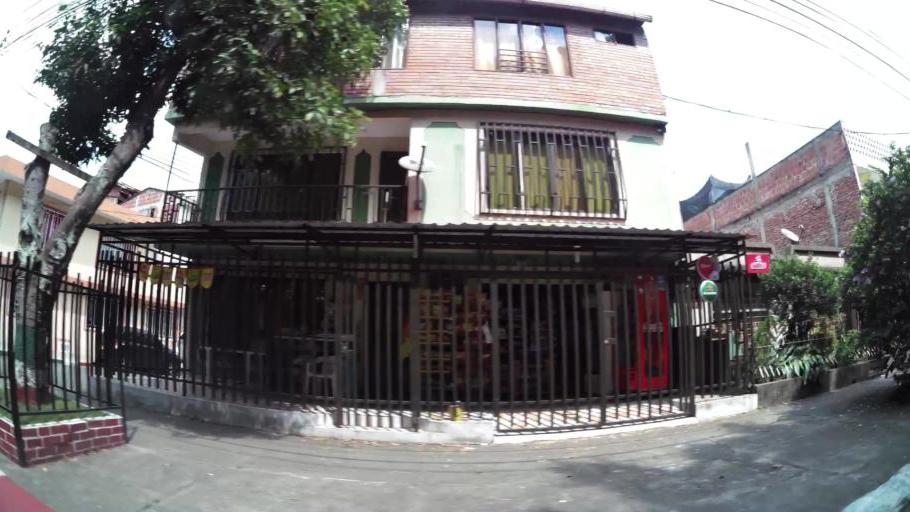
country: CO
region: Valle del Cauca
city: Cali
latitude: 3.4846
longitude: -76.5035
